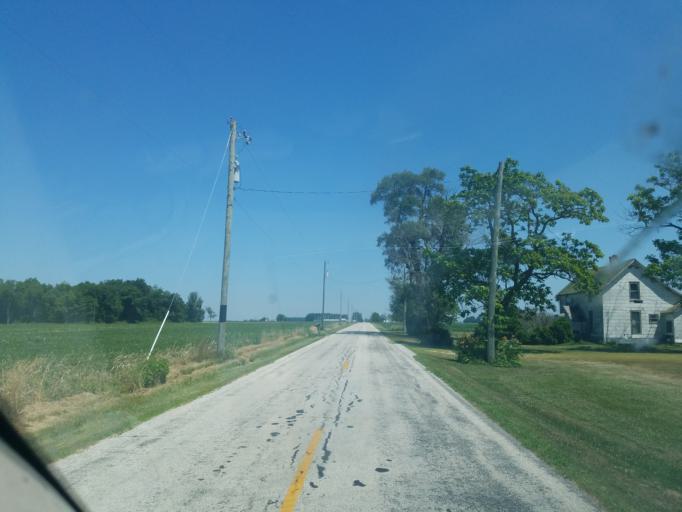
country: US
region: Ohio
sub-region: Mercer County
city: Rockford
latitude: 40.5852
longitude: -84.7084
